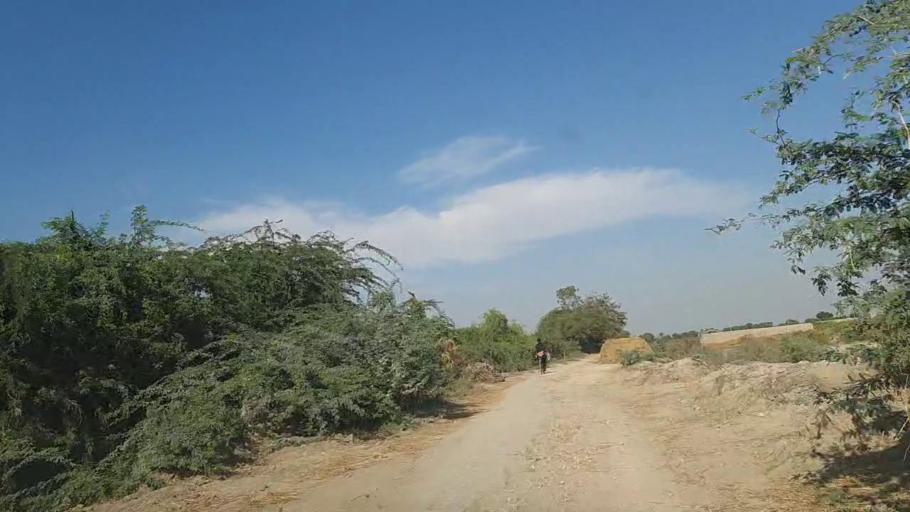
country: PK
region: Sindh
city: Bulri
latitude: 24.8616
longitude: 68.2603
